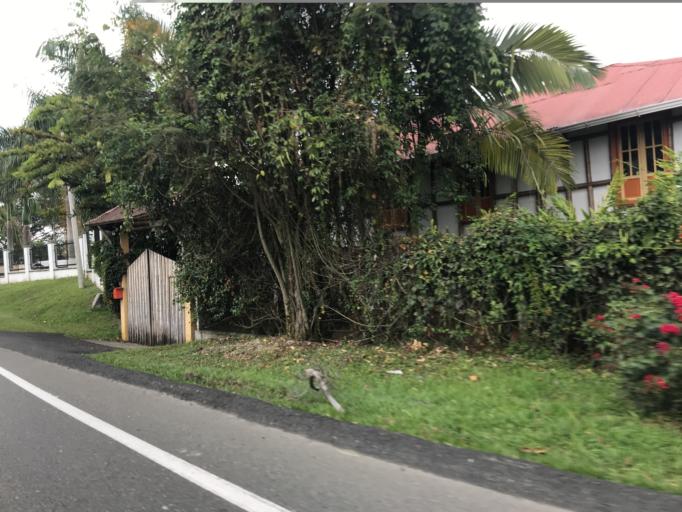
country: CO
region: Quindio
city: Armenia
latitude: 4.4907
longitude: -75.6919
